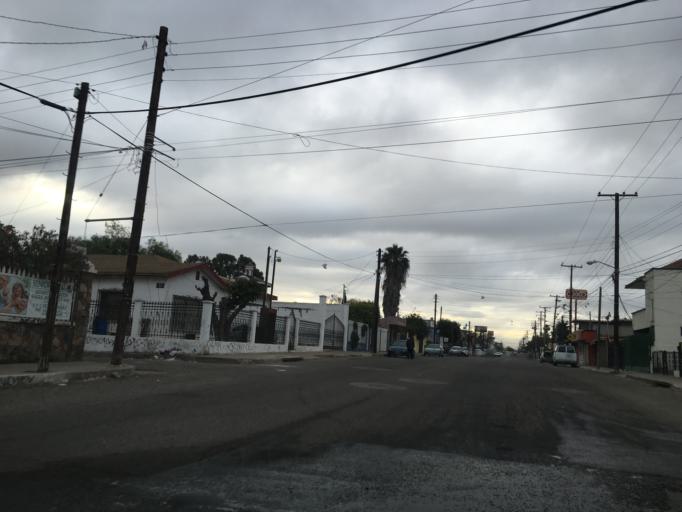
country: MX
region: Baja California
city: Tijuana
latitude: 32.5384
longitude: -117.0587
